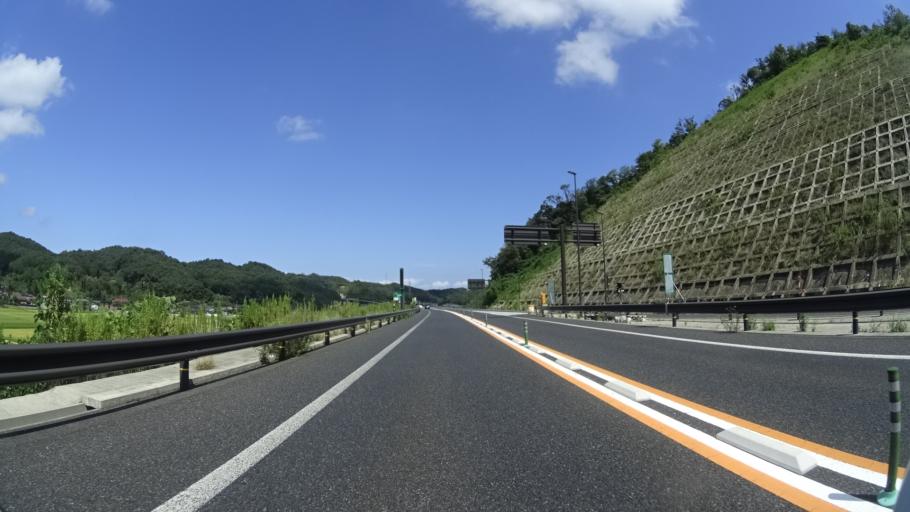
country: JP
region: Tottori
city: Tottori
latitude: 35.4813
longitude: 134.1978
